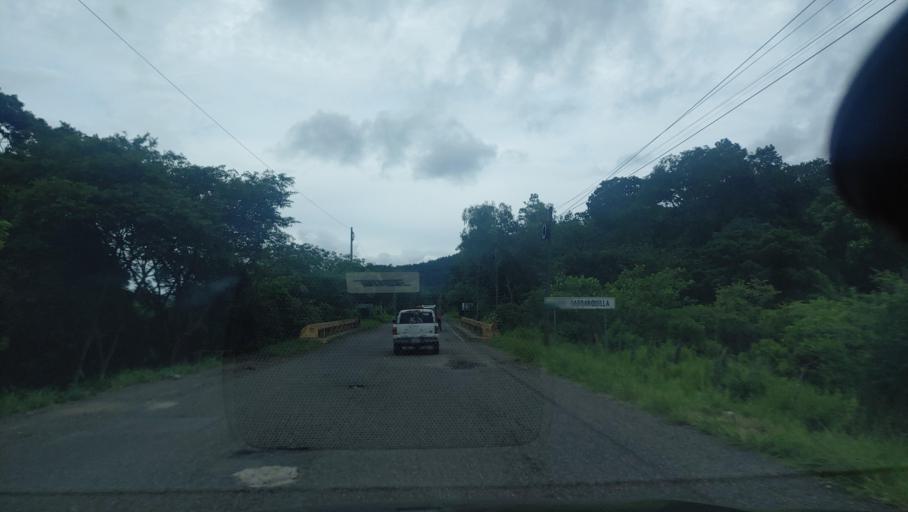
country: HN
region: Choluteca
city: San Marcos de Colon
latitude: 13.3775
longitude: -86.8801
